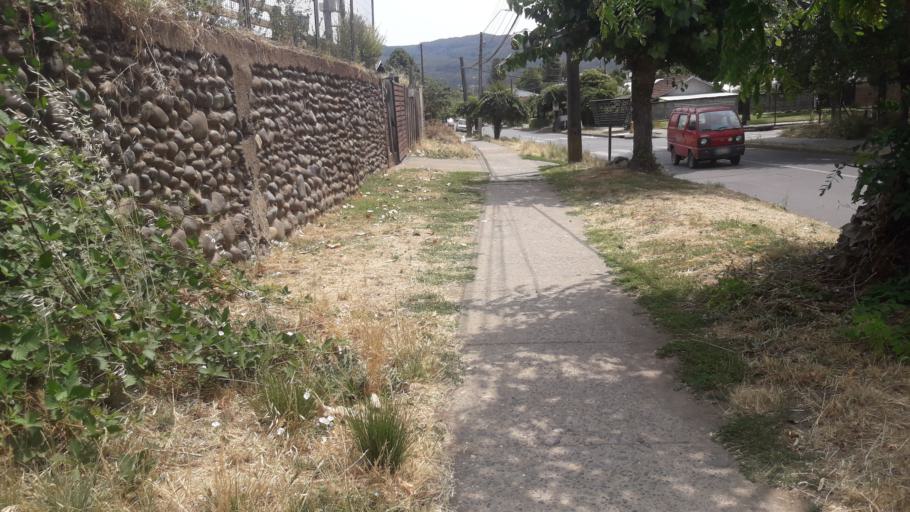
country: CL
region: Biobio
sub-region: Provincia de Biobio
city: Nacimiento
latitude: -37.5043
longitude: -72.6792
